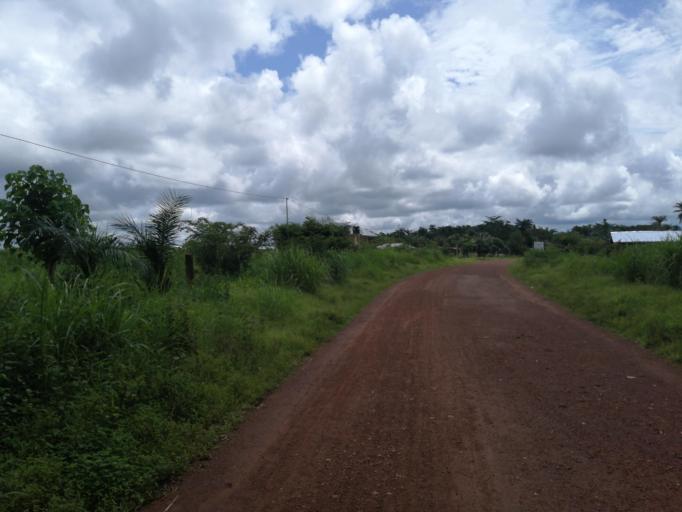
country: SL
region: Northern Province
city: Port Loko
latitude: 8.7866
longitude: -12.7764
